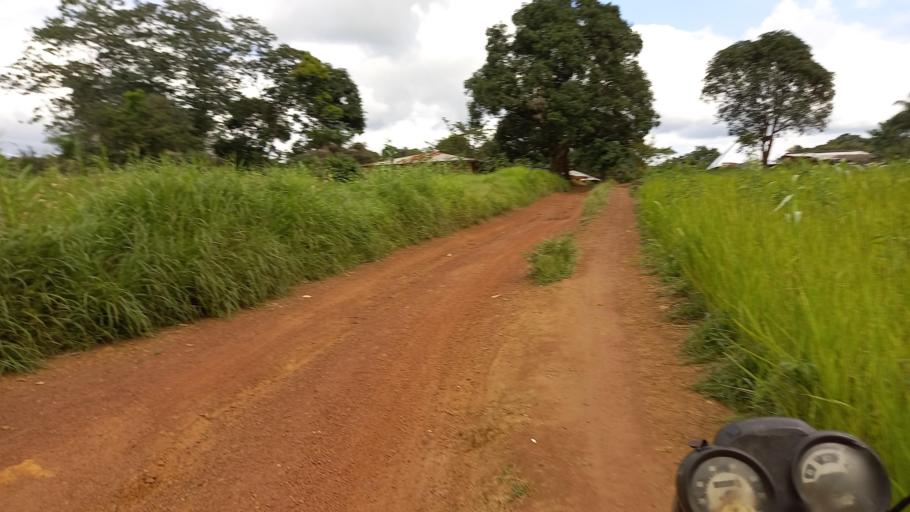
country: SL
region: Northern Province
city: Kamakwie
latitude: 9.5029
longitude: -12.2383
